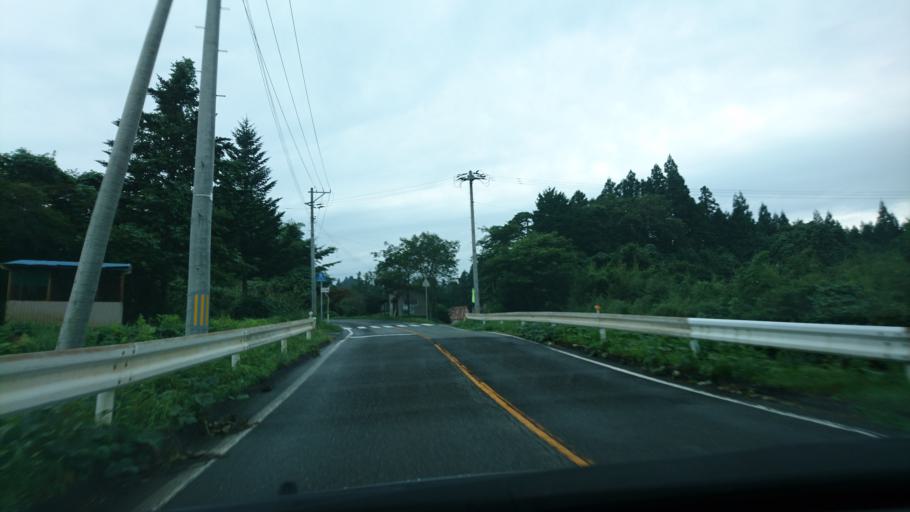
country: JP
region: Iwate
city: Ichinoseki
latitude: 39.0210
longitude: 141.2063
